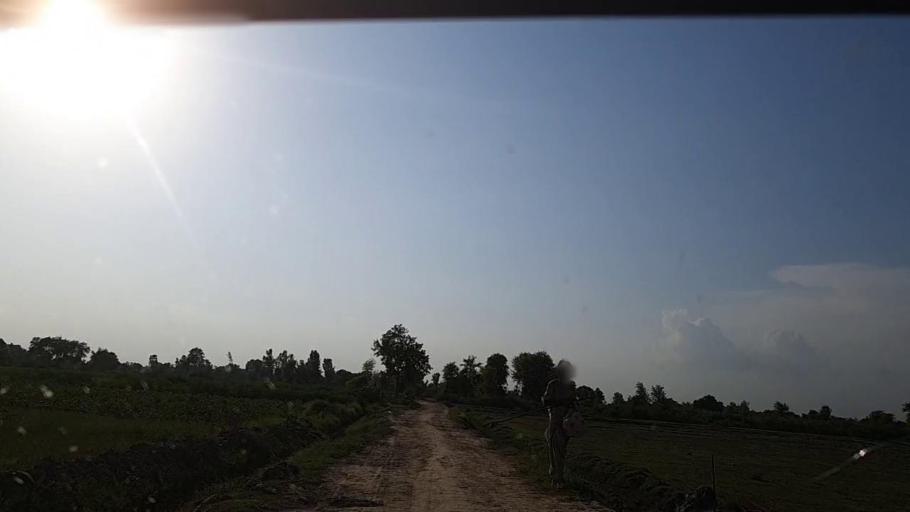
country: PK
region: Sindh
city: Pano Aqil
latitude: 27.9073
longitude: 69.2041
